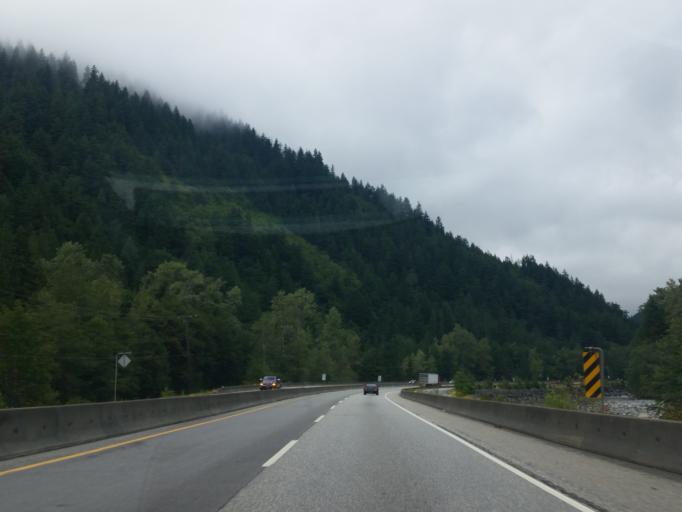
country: CA
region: British Columbia
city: Hope
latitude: 49.3929
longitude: -121.3194
